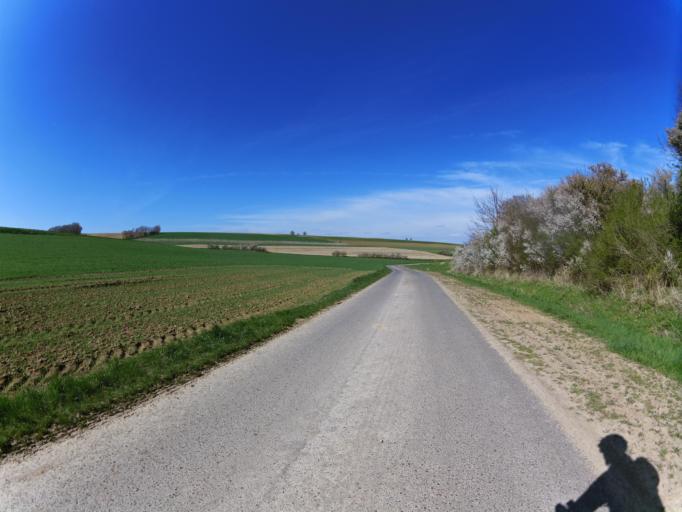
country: DE
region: Bavaria
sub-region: Regierungsbezirk Unterfranken
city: Winterhausen
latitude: 49.6904
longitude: 9.9929
